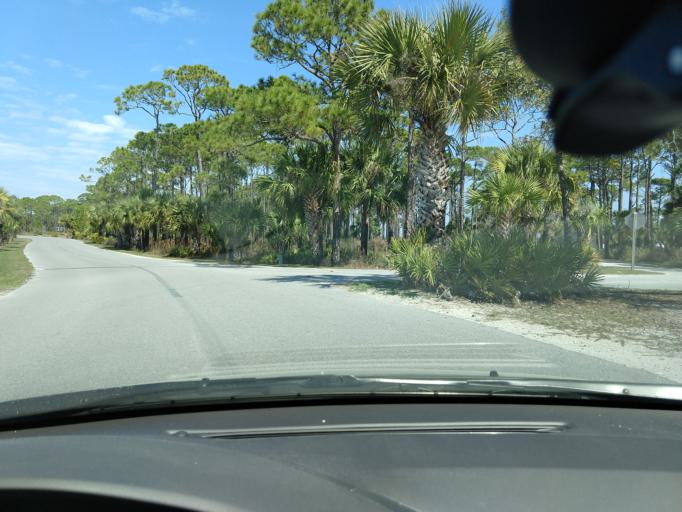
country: US
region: Florida
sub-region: Gulf County
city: Port Saint Joe
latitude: 29.7762
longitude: -85.4038
